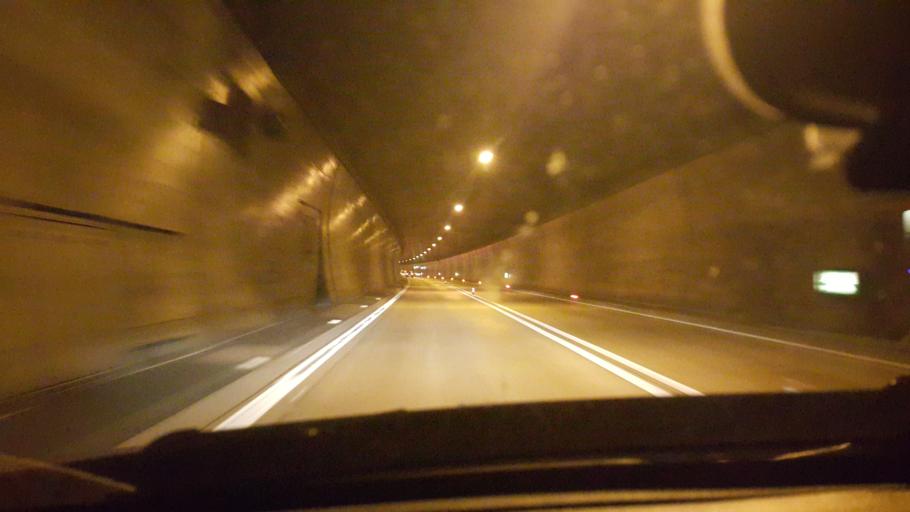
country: AT
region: Styria
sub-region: Graz Stadt
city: Wetzelsdorf
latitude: 47.0584
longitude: 15.3976
